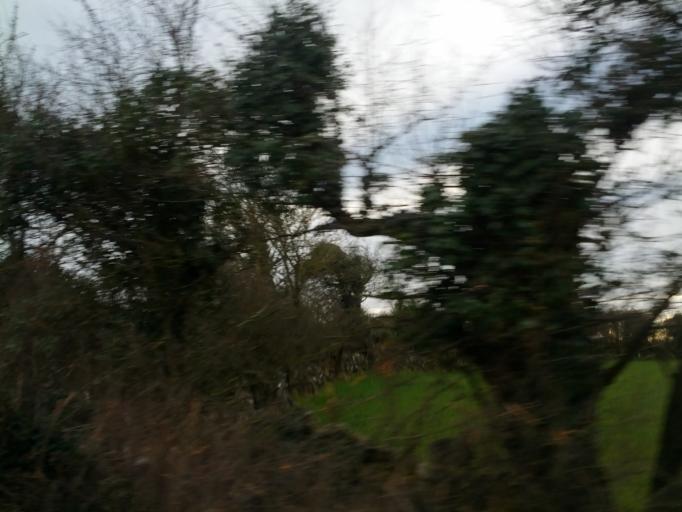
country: IE
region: Connaught
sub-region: County Galway
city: Gort
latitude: 53.1539
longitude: -8.8616
